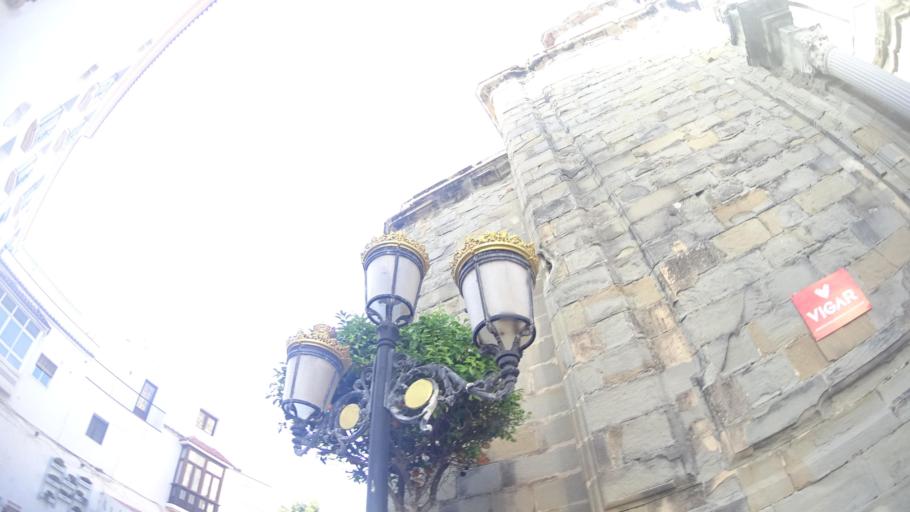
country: ES
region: Andalusia
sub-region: Provincia de Cadiz
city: Tarifa
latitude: 36.0135
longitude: -5.6021
